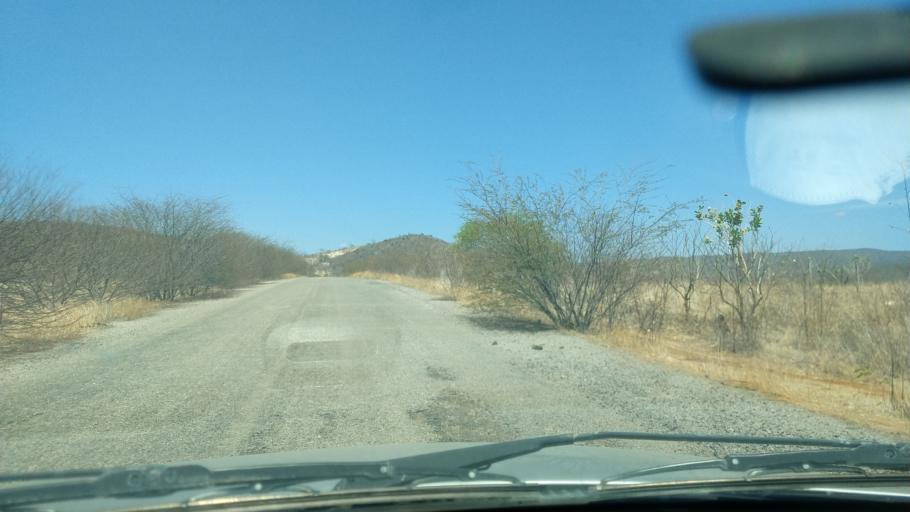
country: BR
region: Rio Grande do Norte
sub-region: Sao Tome
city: Sao Tome
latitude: -5.9736
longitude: -36.1515
